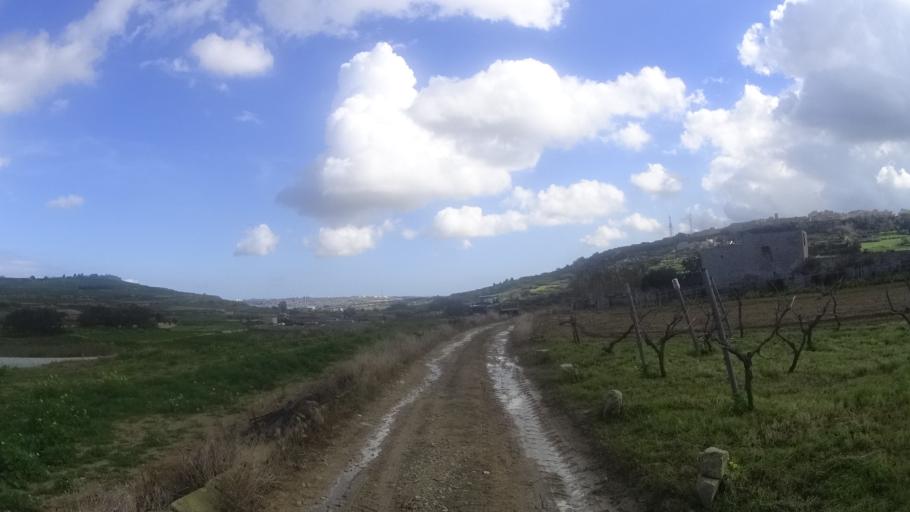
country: MT
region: L-Imtarfa
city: Imtarfa
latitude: 35.8971
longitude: 14.3908
